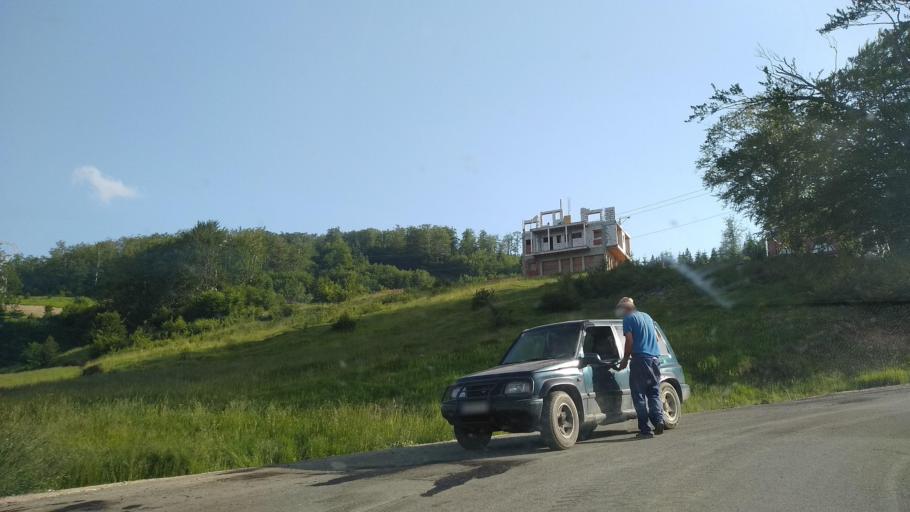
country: RO
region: Hunedoara
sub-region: Municipiul  Vulcan
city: Jiu-Paroseni
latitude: 45.3303
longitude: 23.2882
